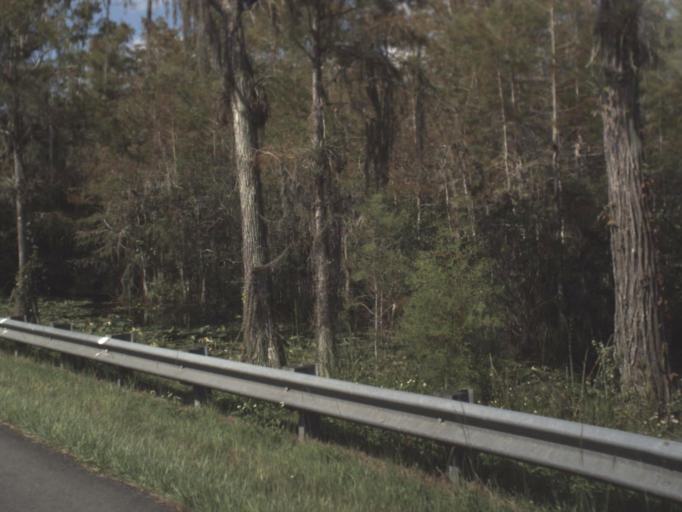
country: US
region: Florida
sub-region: Miami-Dade County
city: Kendall West
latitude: 25.8417
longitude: -80.9153
